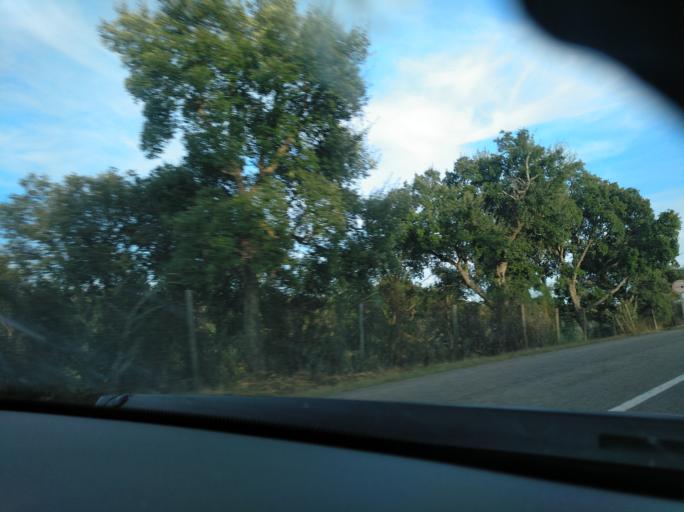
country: PT
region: Portalegre
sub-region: Avis
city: Avis
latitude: 38.8710
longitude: -7.8240
